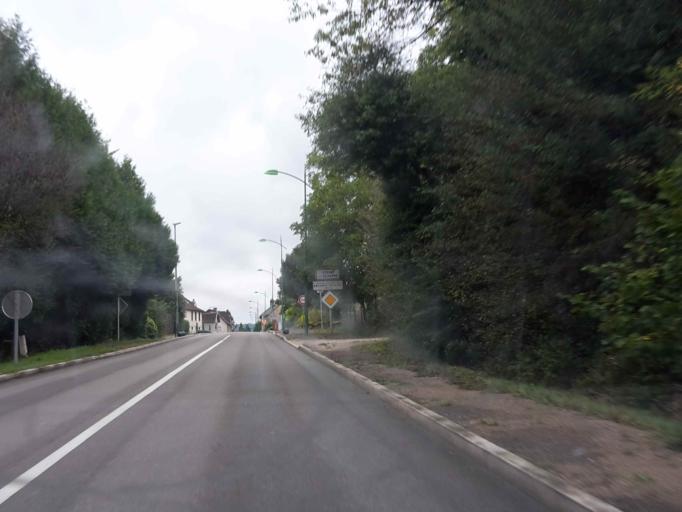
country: FR
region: Franche-Comte
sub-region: Departement du Doubs
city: Novillars
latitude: 47.2773
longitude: 6.1188
